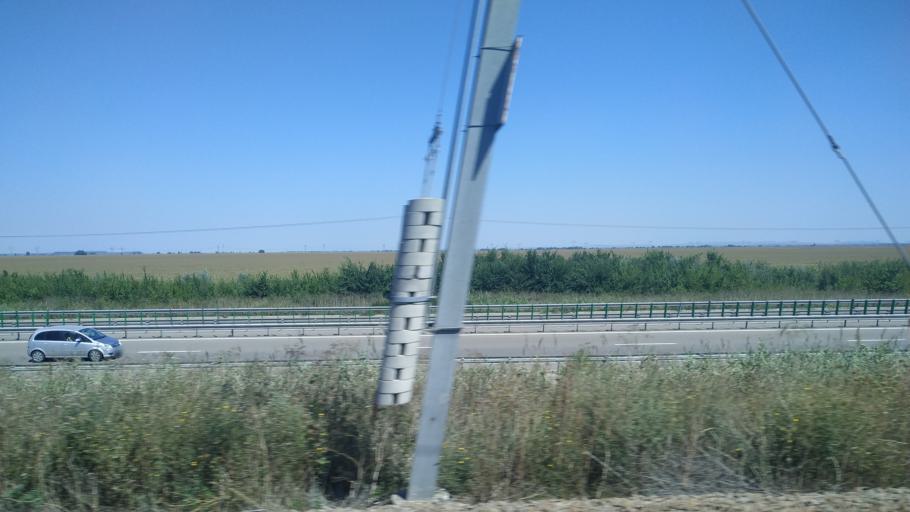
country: RO
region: Constanta
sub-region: Oras Cernavoda
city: Cernavoda
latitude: 44.3555
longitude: 27.9555
